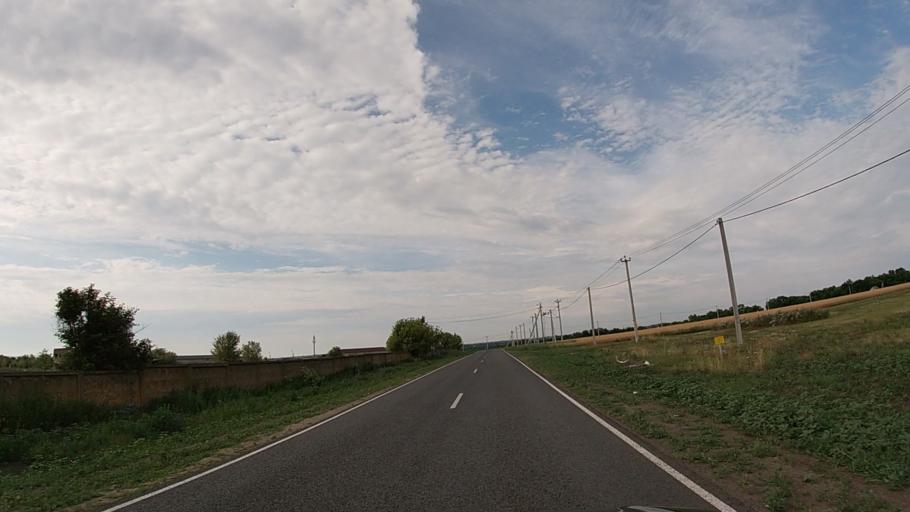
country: RU
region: Belgorod
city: Severnyy
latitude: 50.7237
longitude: 36.5845
